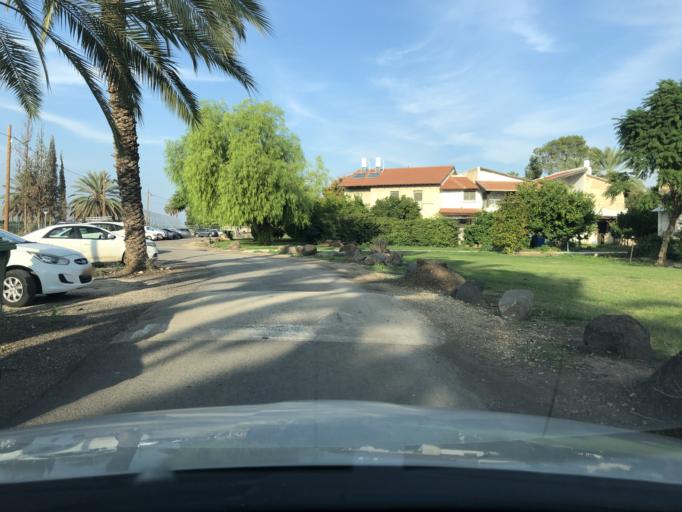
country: IL
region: Northern District
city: Yavne'el
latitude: 32.6603
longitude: 35.5788
